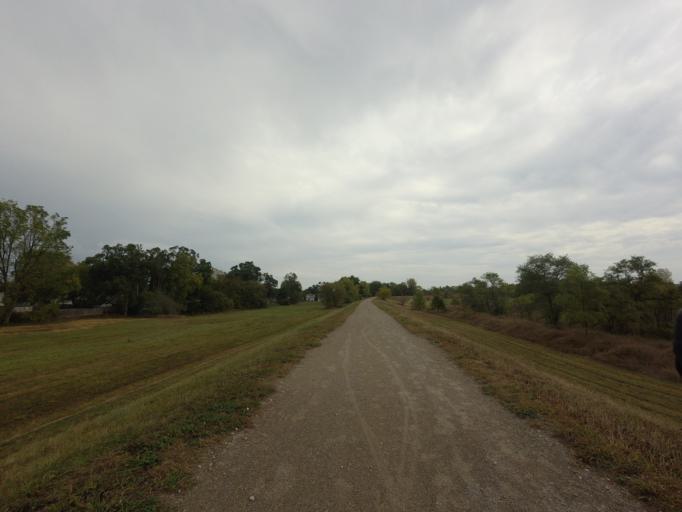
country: CA
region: Ontario
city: Brantford
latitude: 43.1214
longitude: -80.2445
